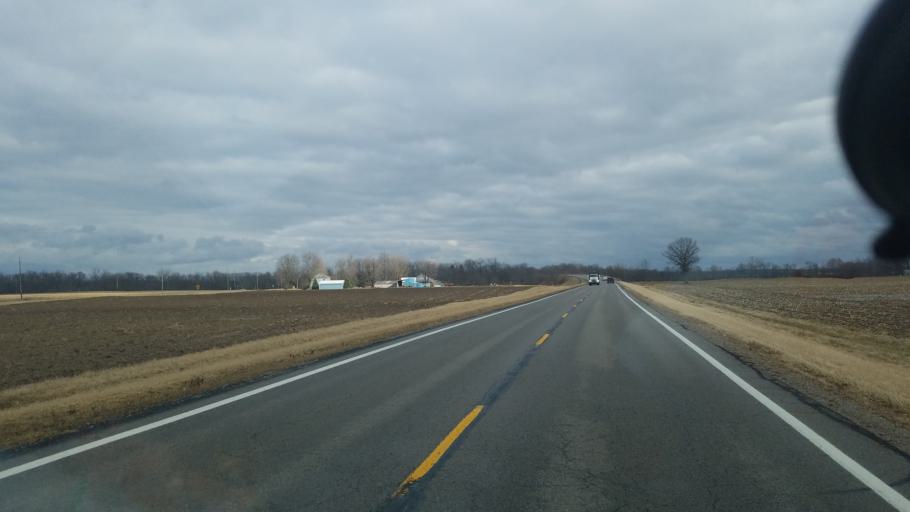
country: US
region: Ohio
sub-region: Morrow County
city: Mount Gilead
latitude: 40.6484
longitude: -82.9044
